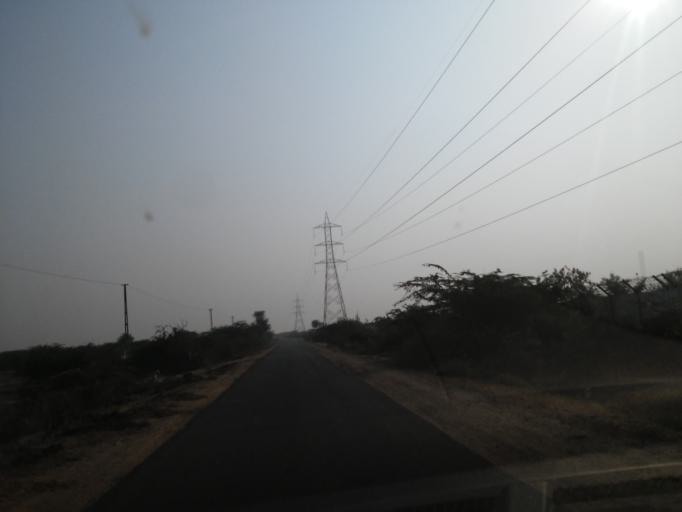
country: IN
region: Gujarat
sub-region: Kachchh
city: Mandvi
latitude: 22.8325
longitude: 69.5019
